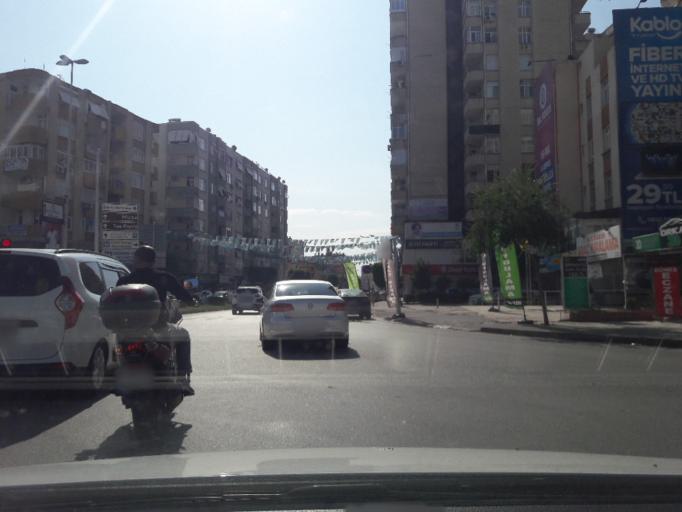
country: TR
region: Adana
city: Adana
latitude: 37.0159
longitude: 35.3220
